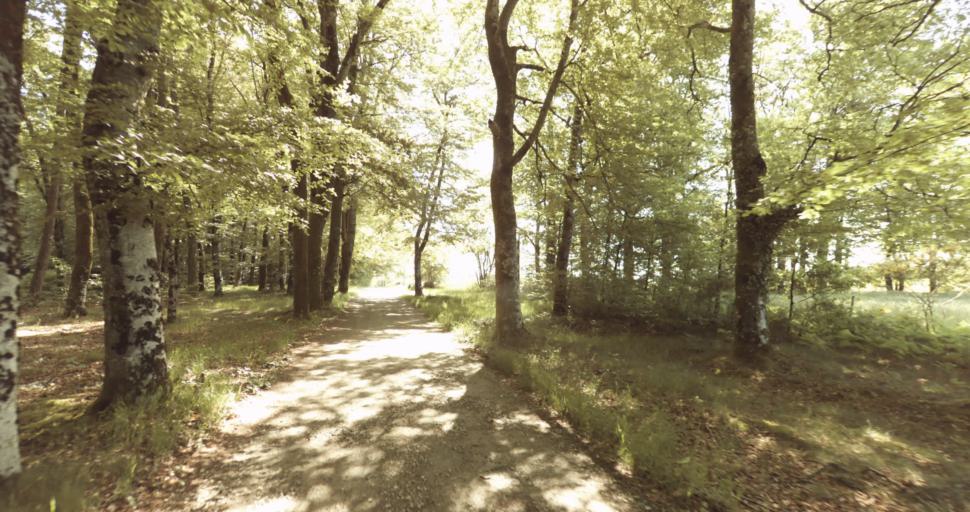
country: FR
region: Limousin
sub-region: Departement de la Haute-Vienne
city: Solignac
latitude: 45.7235
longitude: 1.2581
